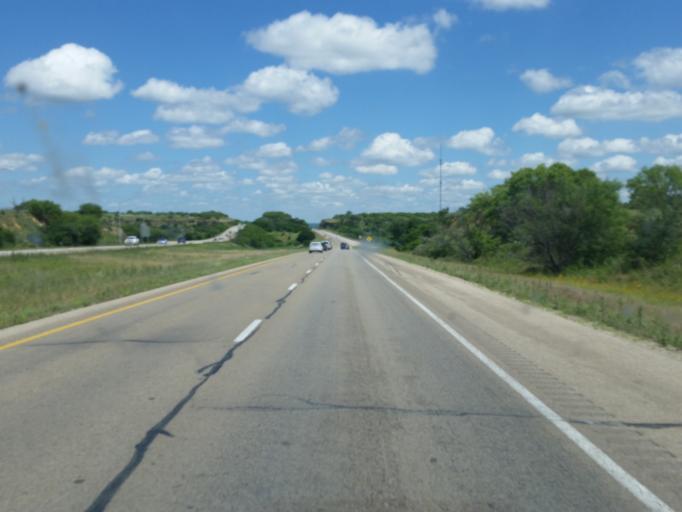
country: US
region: Texas
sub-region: Callahan County
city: Baird
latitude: 32.3976
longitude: -99.3719
